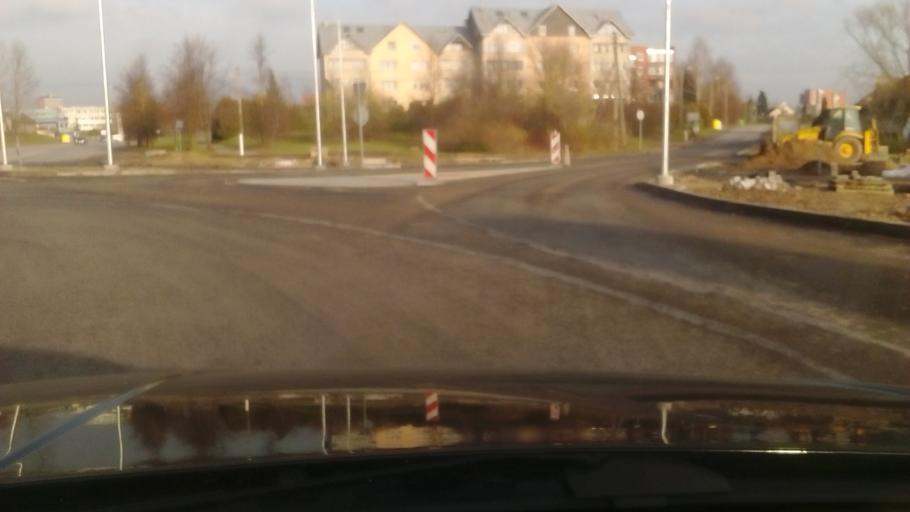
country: LT
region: Alytaus apskritis
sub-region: Alytus
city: Alytus
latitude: 54.4091
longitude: 24.0049
